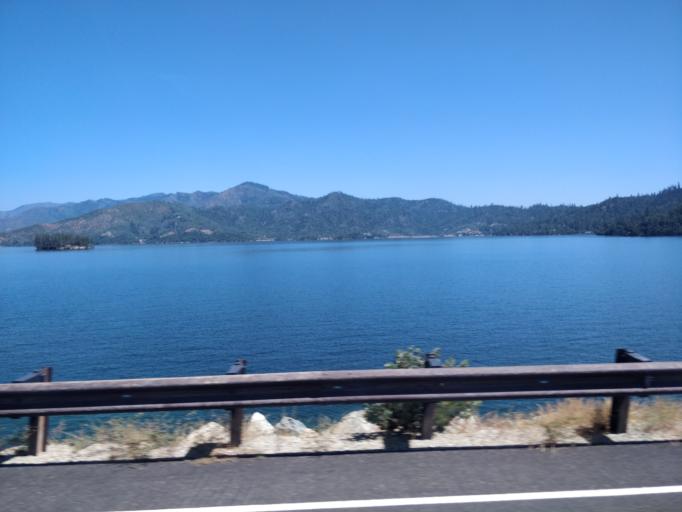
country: US
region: California
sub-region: Shasta County
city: Shasta
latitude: 40.5980
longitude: -122.5459
